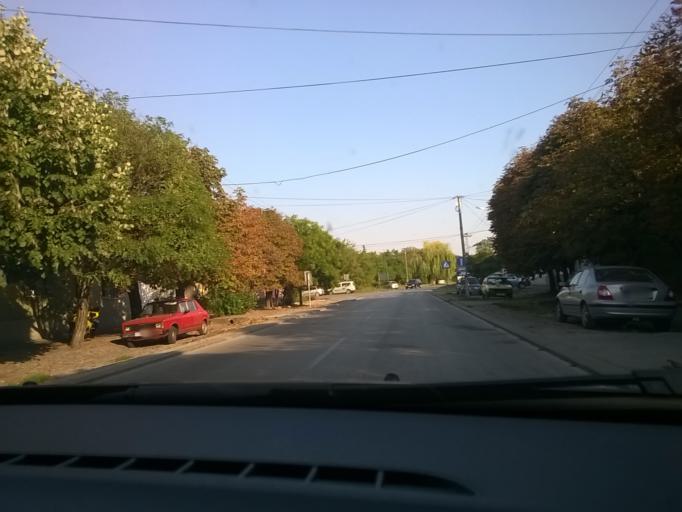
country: RS
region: Autonomna Pokrajina Vojvodina
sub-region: Juznobanatski Okrug
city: Vrsac
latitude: 45.1125
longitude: 21.3070
